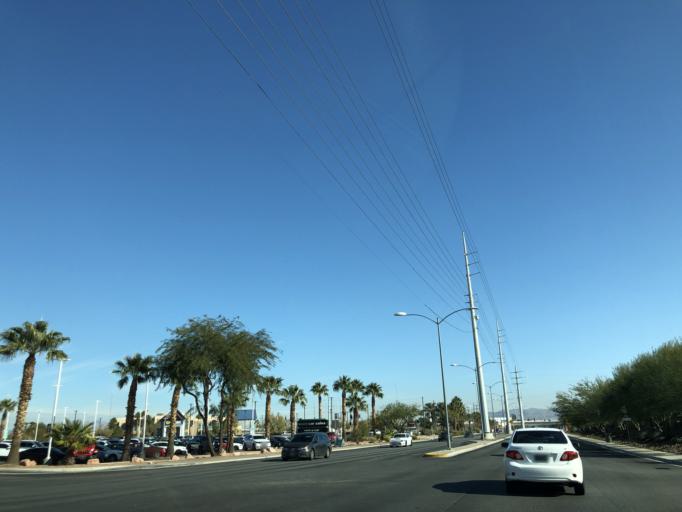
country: US
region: Nevada
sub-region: Clark County
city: Whitney
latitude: 36.0563
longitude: -115.0334
